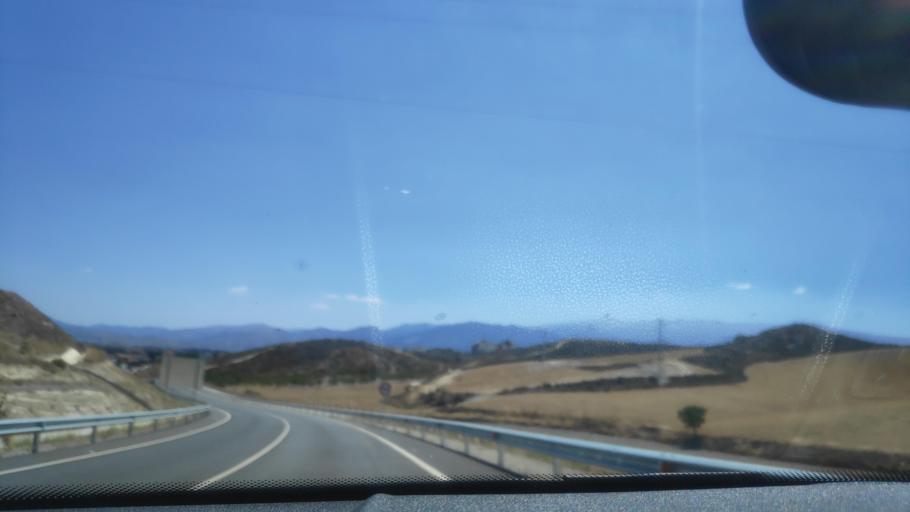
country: ES
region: Andalusia
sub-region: Provincia de Granada
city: Alhendin
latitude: 37.1026
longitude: -3.6707
